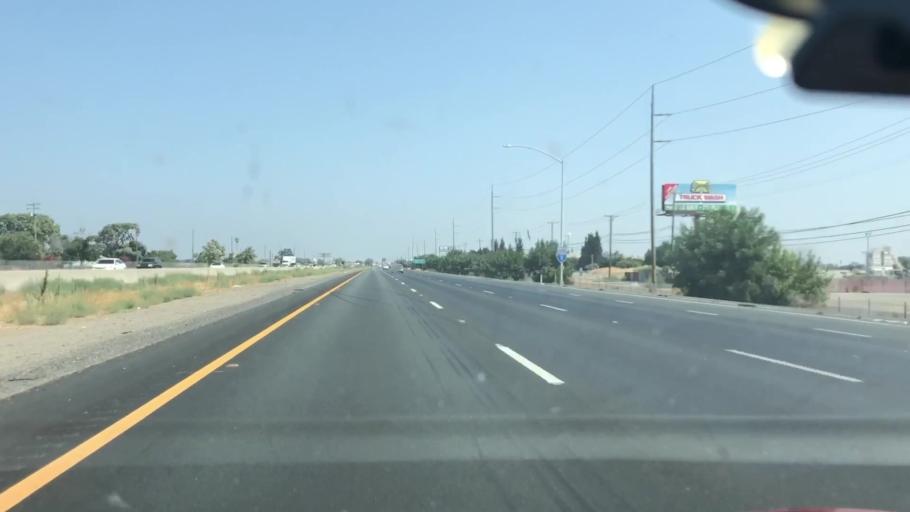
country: US
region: California
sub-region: San Joaquin County
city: French Camp
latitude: 37.8594
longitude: -121.2808
